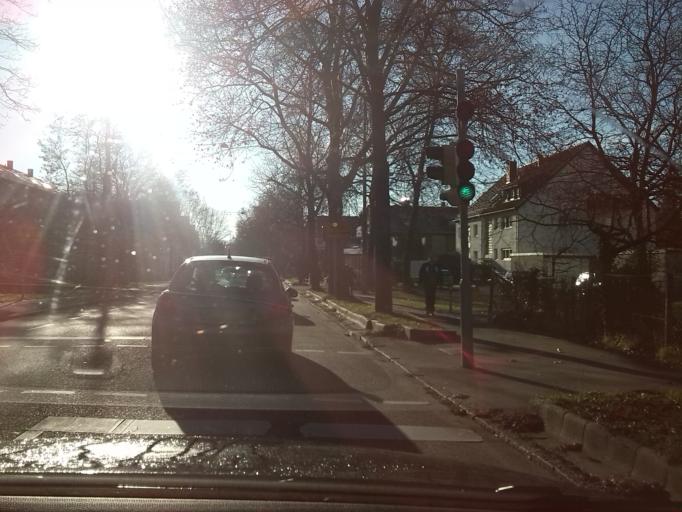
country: DE
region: Baden-Wuerttemberg
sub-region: Regierungsbezirk Stuttgart
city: Fellbach
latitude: 48.7901
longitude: 9.2594
